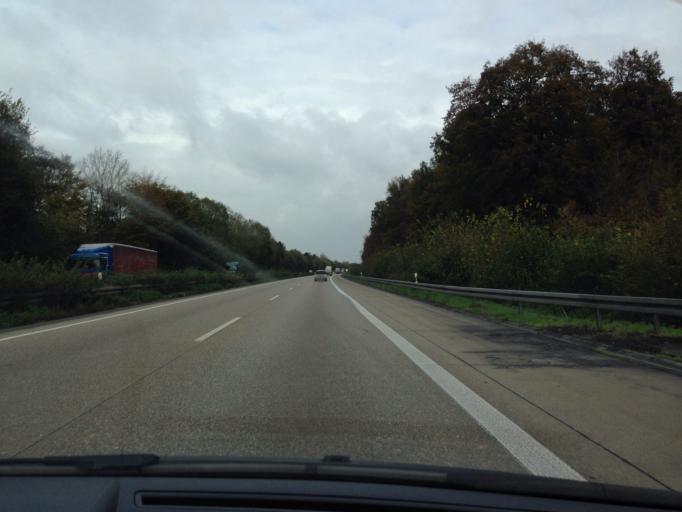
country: DE
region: North Rhine-Westphalia
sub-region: Regierungsbezirk Munster
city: Senden
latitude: 51.8542
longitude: 7.5784
